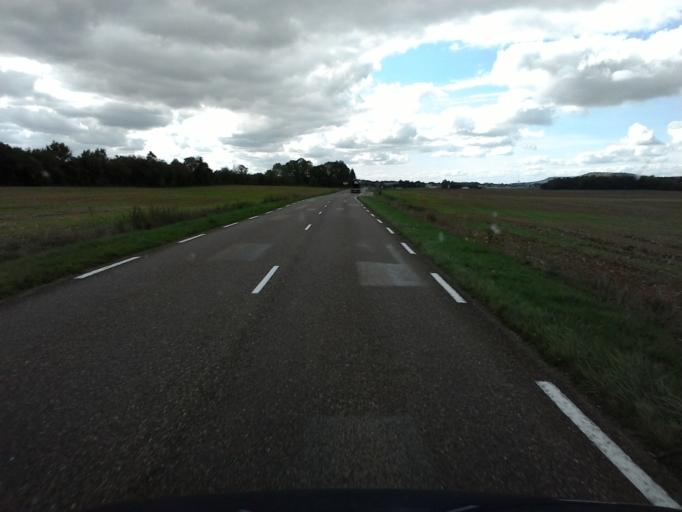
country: FR
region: Lorraine
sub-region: Departement des Vosges
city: Liffol-le-Grand
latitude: 48.3063
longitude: 5.5594
